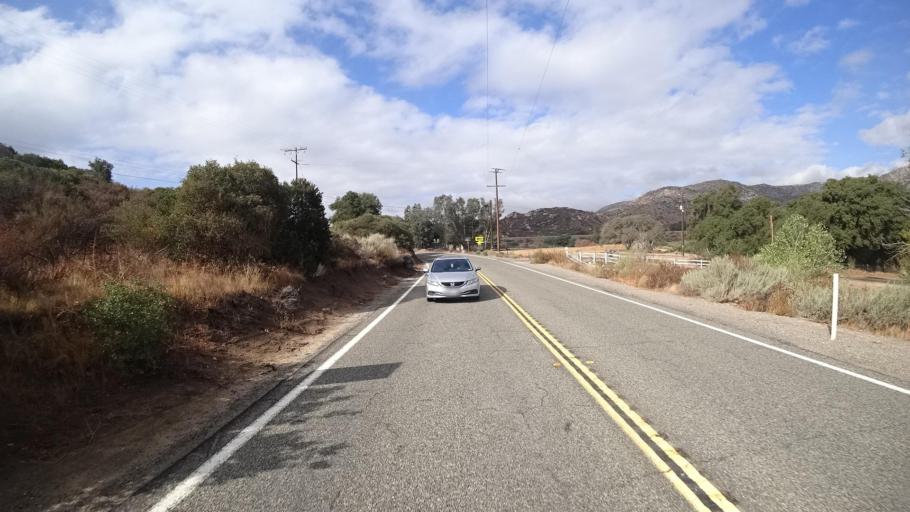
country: MX
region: Baja California
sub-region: Tecate
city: Hacienda Tecate
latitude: 32.5972
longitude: -116.5064
